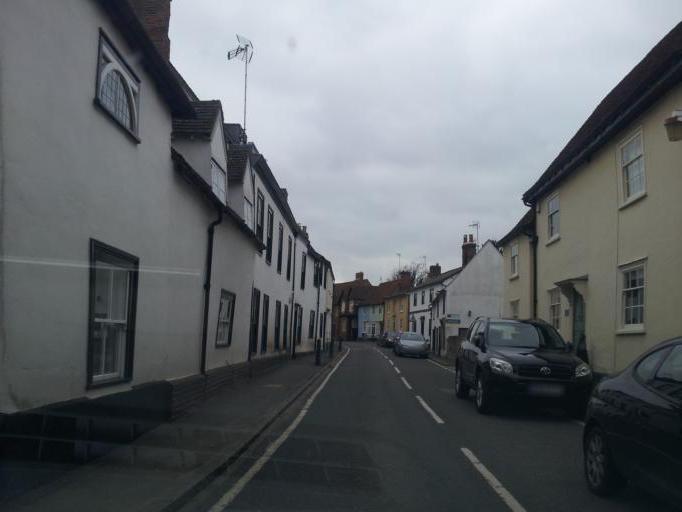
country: GB
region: England
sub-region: Hertfordshire
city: Great Munden
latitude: 51.8927
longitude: 0.0136
